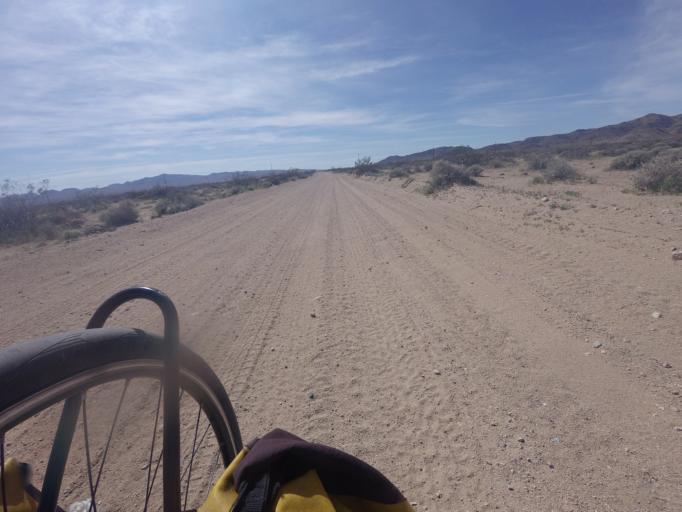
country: US
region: California
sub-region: San Bernardino County
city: Searles Valley
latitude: 35.5718
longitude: -117.4406
